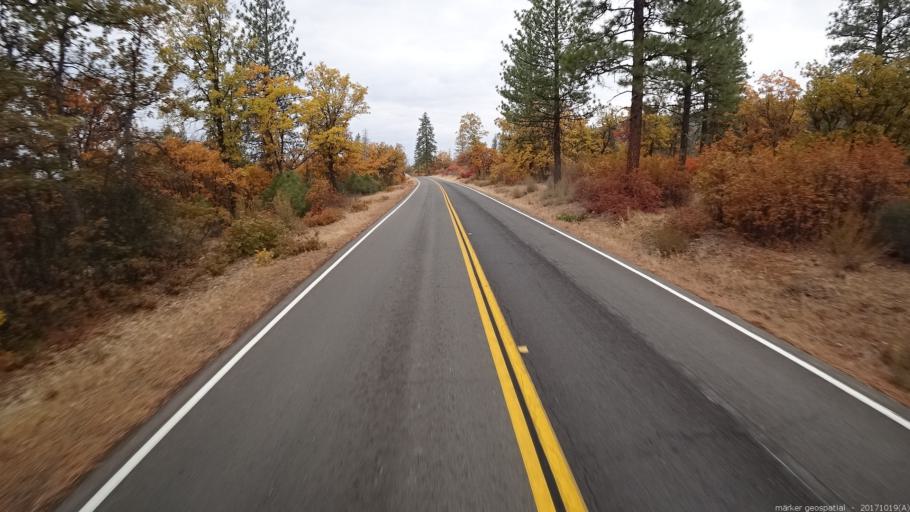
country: US
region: California
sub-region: Shasta County
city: Burney
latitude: 41.1455
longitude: -121.3489
